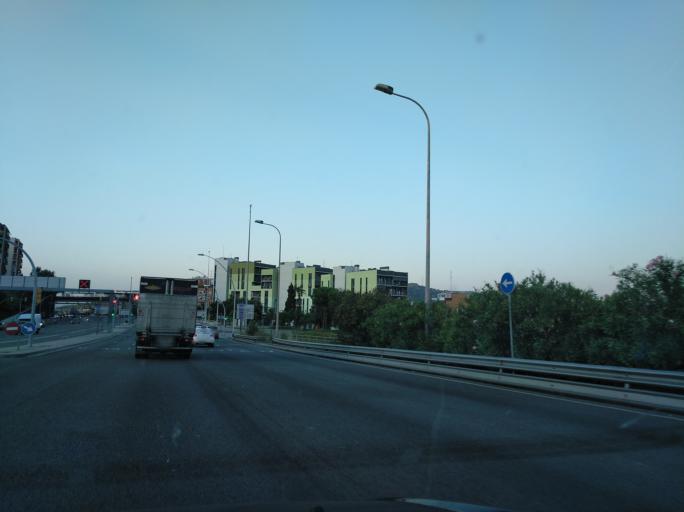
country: ES
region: Catalonia
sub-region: Provincia de Barcelona
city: Nou Barris
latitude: 41.4483
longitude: 2.1883
